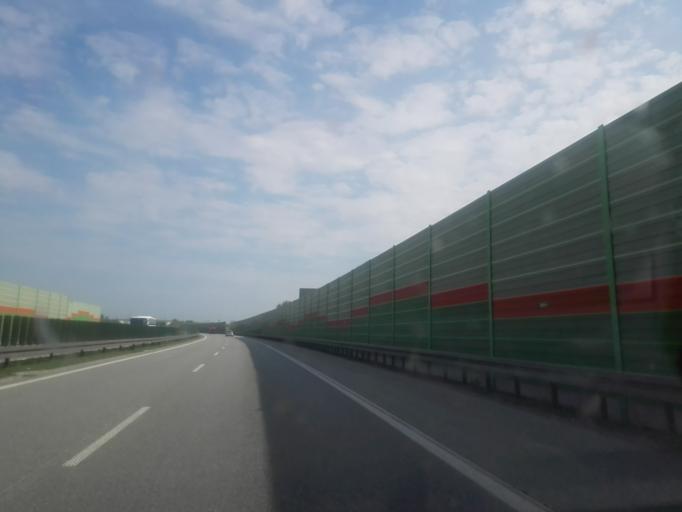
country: PL
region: Lodz Voivodeship
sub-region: Powiat rawski
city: Rawa Mazowiecka
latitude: 51.7669
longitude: 20.2712
